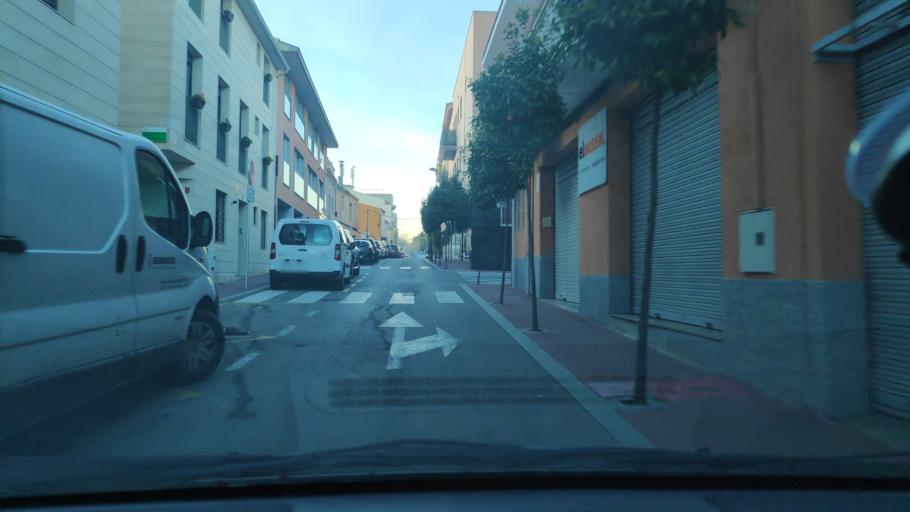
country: ES
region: Catalonia
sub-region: Provincia de Barcelona
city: Sant Quirze del Valles
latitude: 41.5342
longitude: 2.0792
